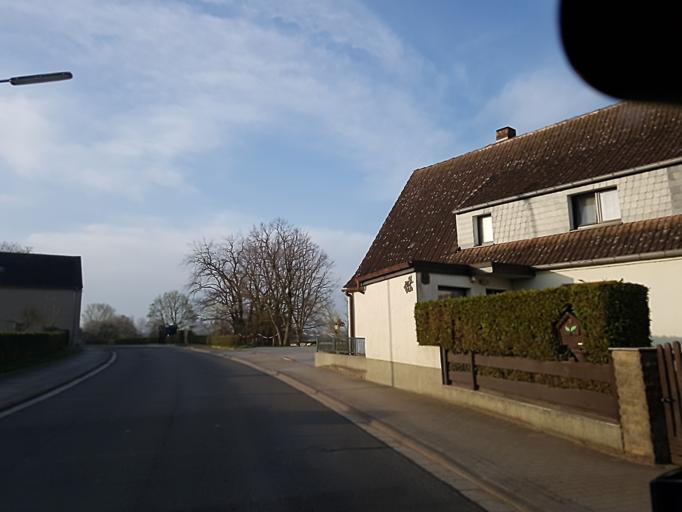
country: DE
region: Brandenburg
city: Muhlberg
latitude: 51.4206
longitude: 13.2656
